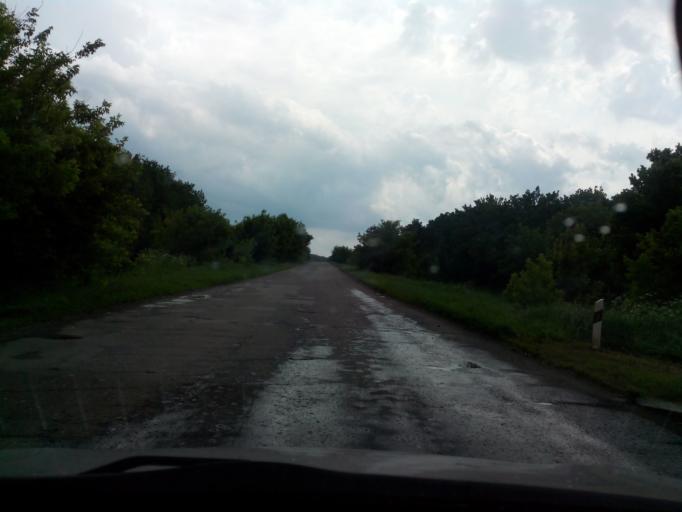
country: RU
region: Volgograd
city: Mikhaylovka
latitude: 49.9103
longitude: 42.9502
